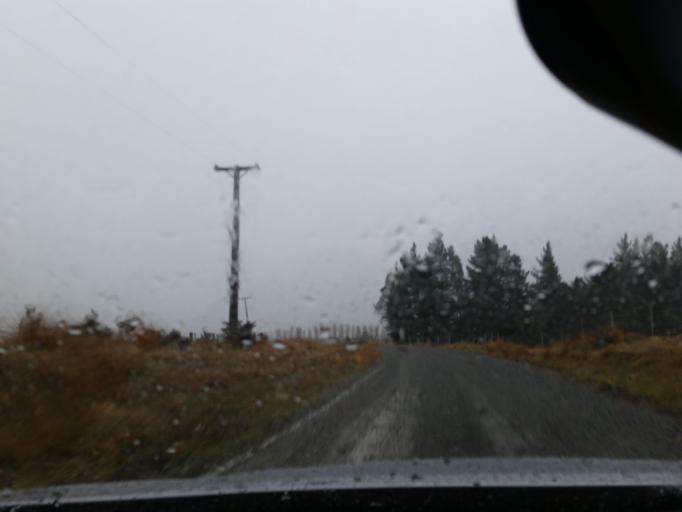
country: NZ
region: Southland
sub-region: Southland District
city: Te Anau
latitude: -45.5708
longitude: 168.0636
